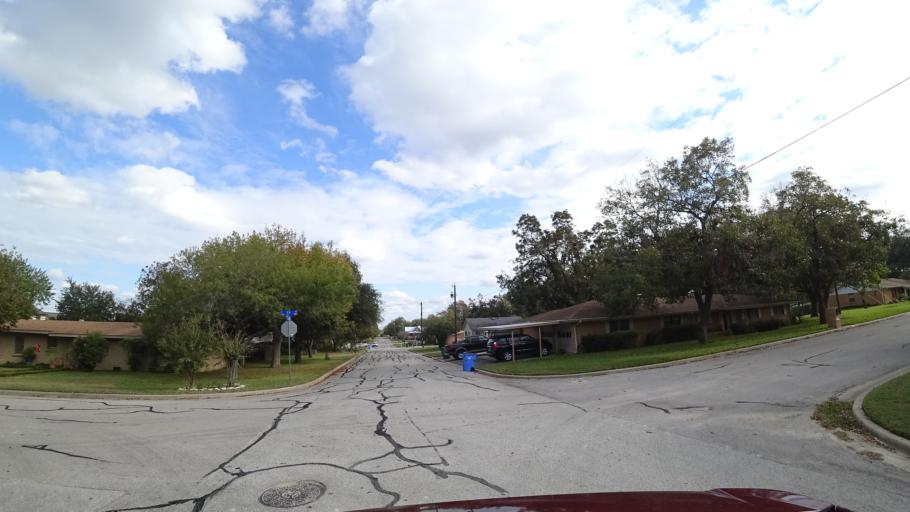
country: US
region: Texas
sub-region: Travis County
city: Pflugerville
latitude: 30.4406
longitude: -97.6246
